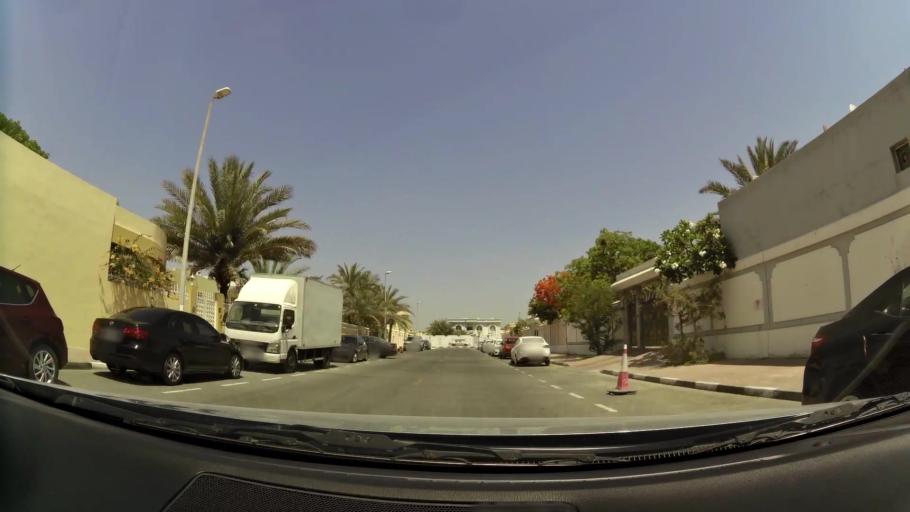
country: AE
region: Dubai
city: Dubai
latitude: 25.2138
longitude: 55.2724
